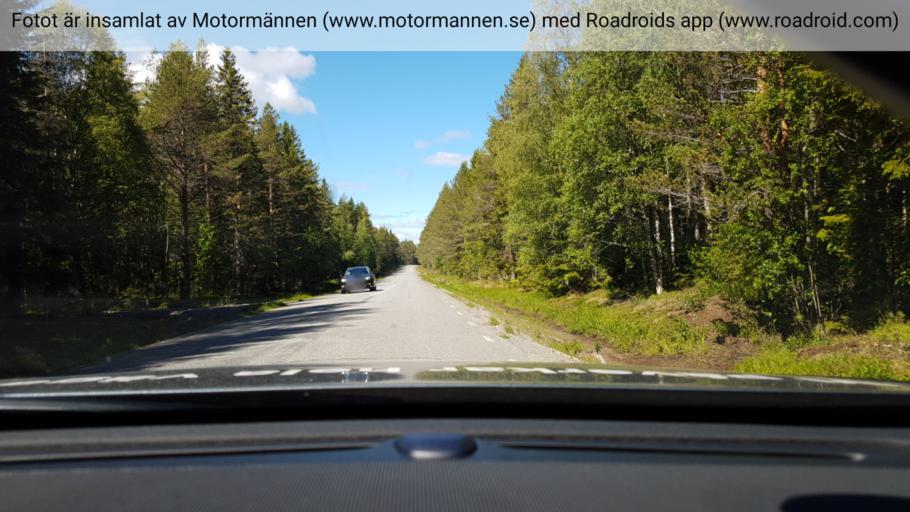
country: SE
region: Vaesterbotten
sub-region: Skelleftea Kommun
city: Burea
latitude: 64.4408
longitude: 21.4968
